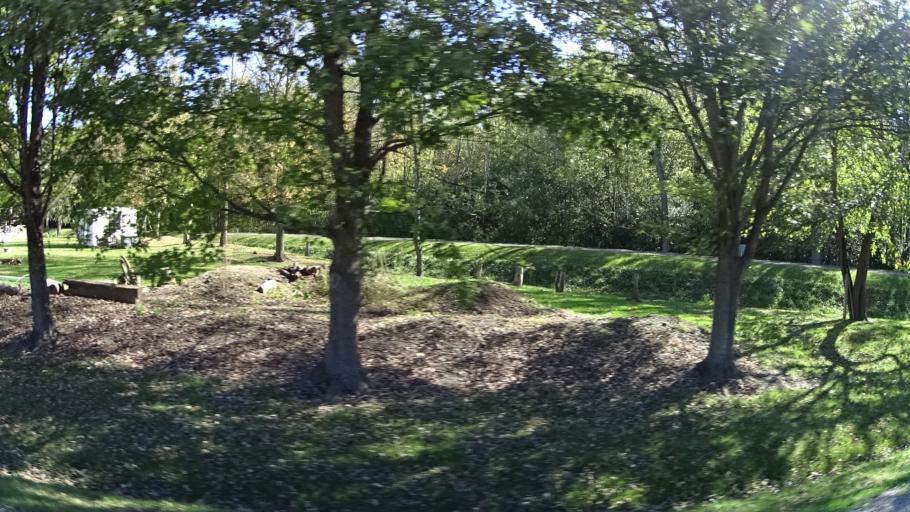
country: US
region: Ohio
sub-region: Lorain County
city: Oberlin
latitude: 41.2984
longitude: -82.1970
